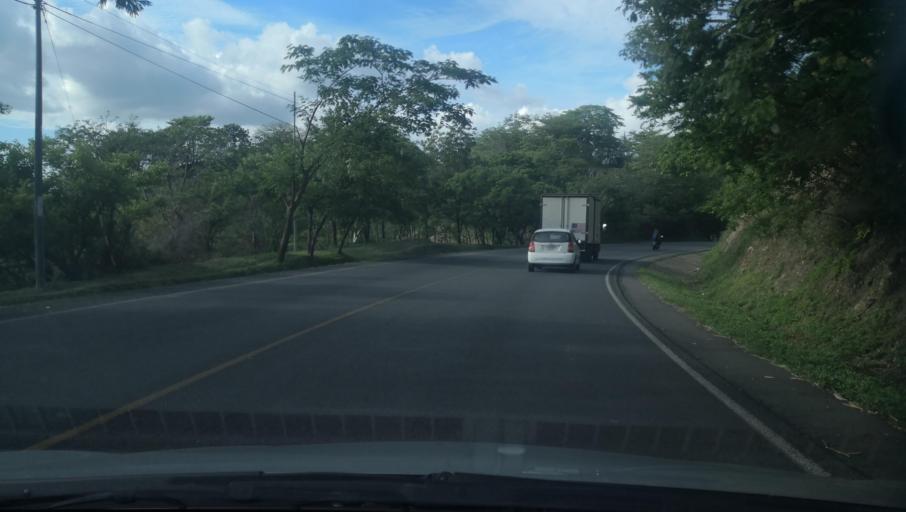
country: NI
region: Nueva Segovia
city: Ocotal
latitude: 13.5963
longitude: -86.4725
